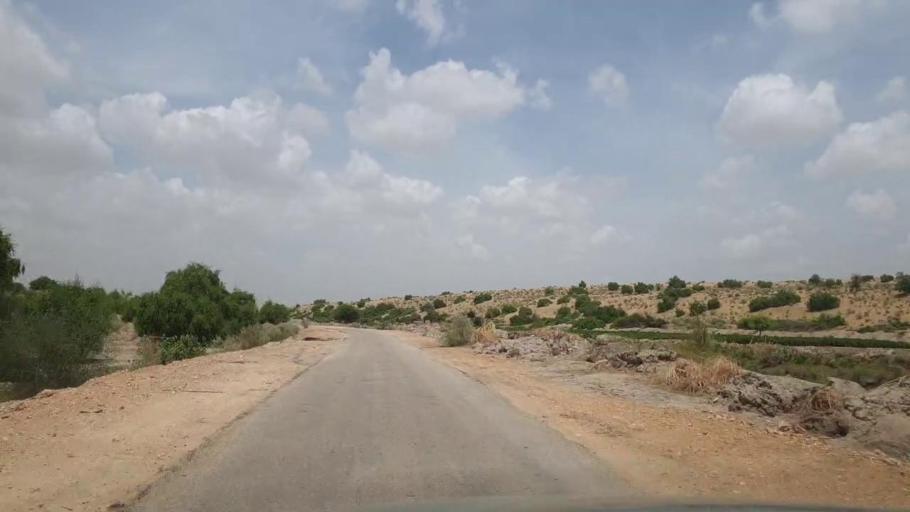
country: PK
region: Sindh
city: Kot Diji
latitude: 27.2111
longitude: 69.0968
